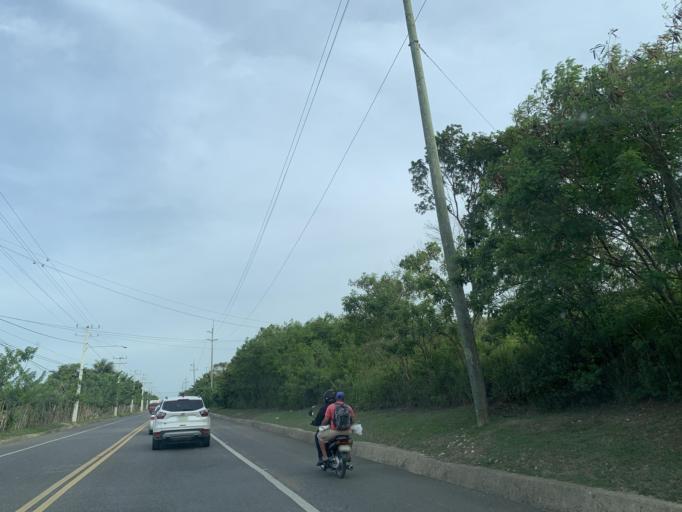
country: DO
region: Puerto Plata
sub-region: Puerto Plata
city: Puerto Plata
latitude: 19.7324
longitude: -70.6277
